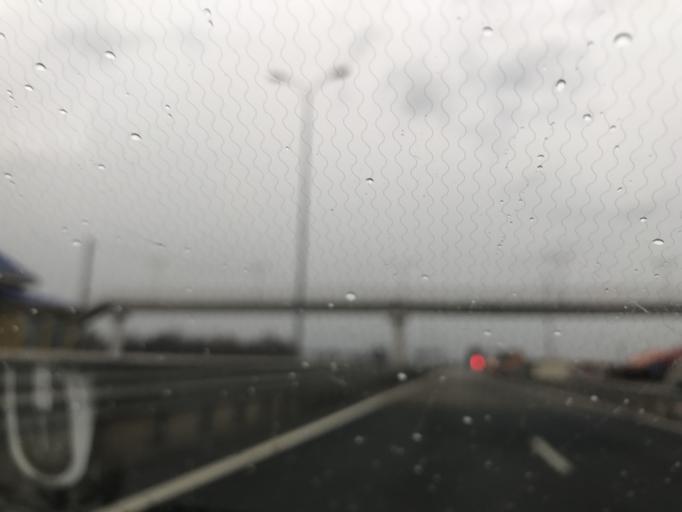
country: RU
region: Krasnodarskiy
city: Pavlovskaya
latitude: 46.1244
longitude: 39.8646
